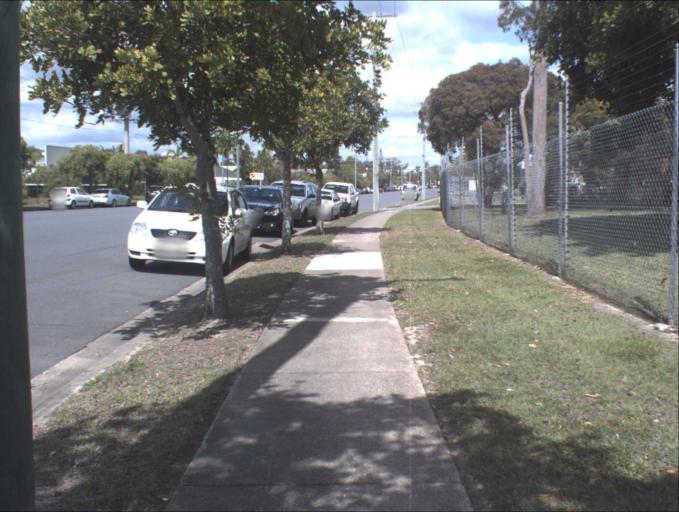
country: AU
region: Queensland
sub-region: Logan
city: Logan Reserve
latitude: -27.6791
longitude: 153.0785
